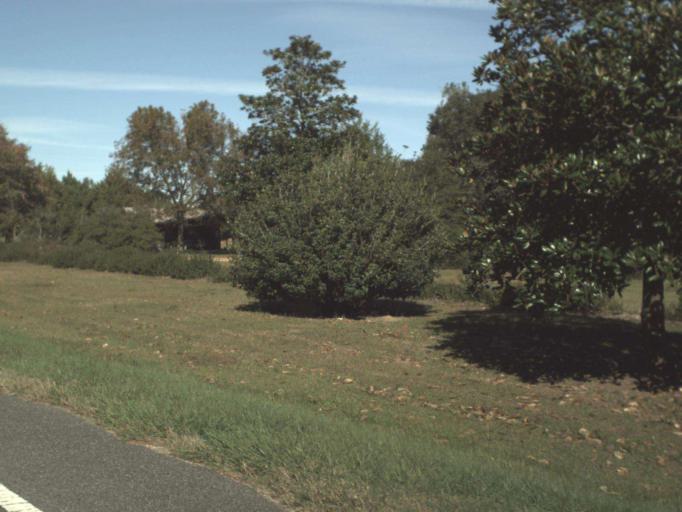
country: US
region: Florida
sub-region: Okaloosa County
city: Crestview
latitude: 30.8051
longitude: -86.7043
